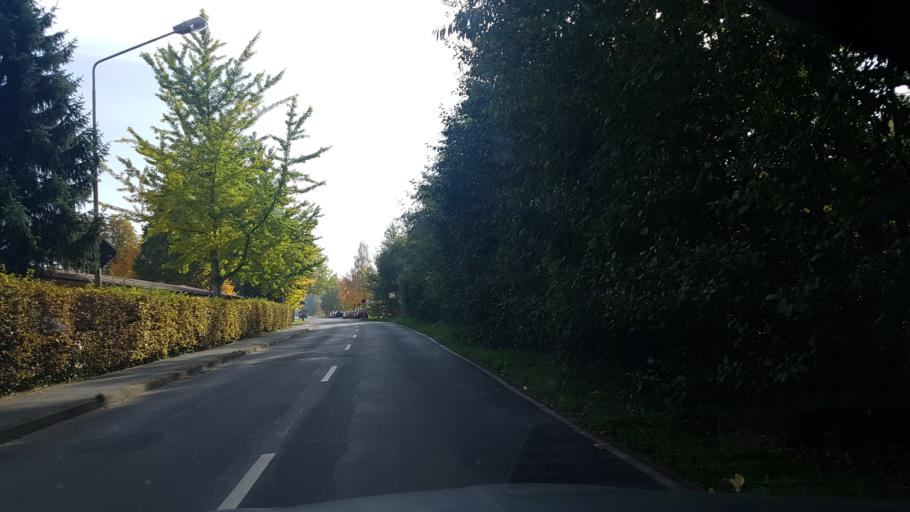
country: DE
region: Saxony
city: Dohma
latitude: 50.9298
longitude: 13.9518
